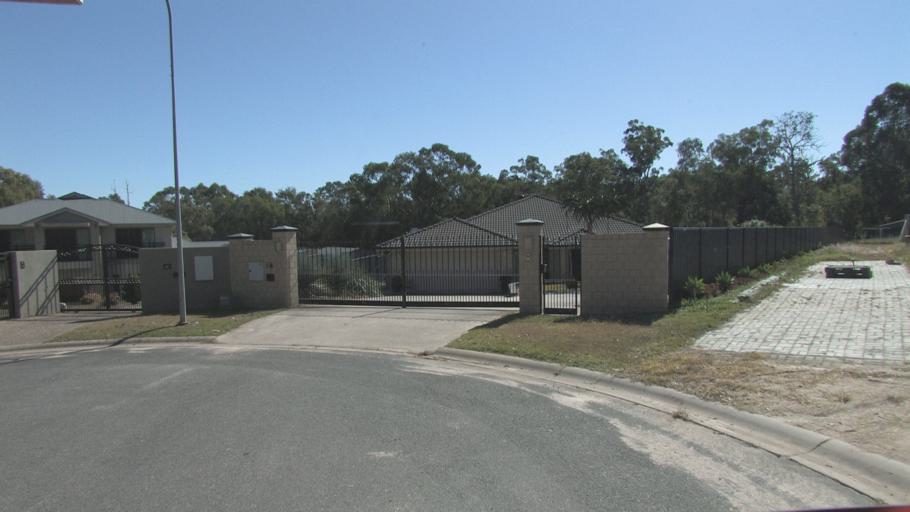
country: AU
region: Queensland
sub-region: Logan
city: Park Ridge South
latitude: -27.6846
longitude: 153.0106
